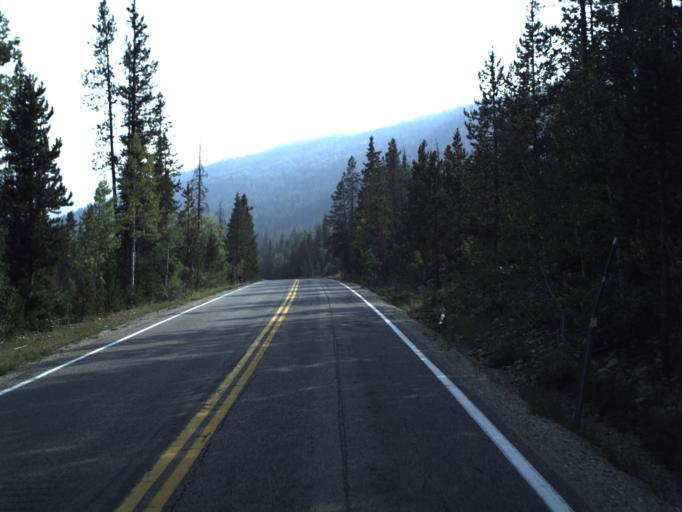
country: US
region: Utah
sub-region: Summit County
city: Kamas
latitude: 40.6277
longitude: -110.9594
